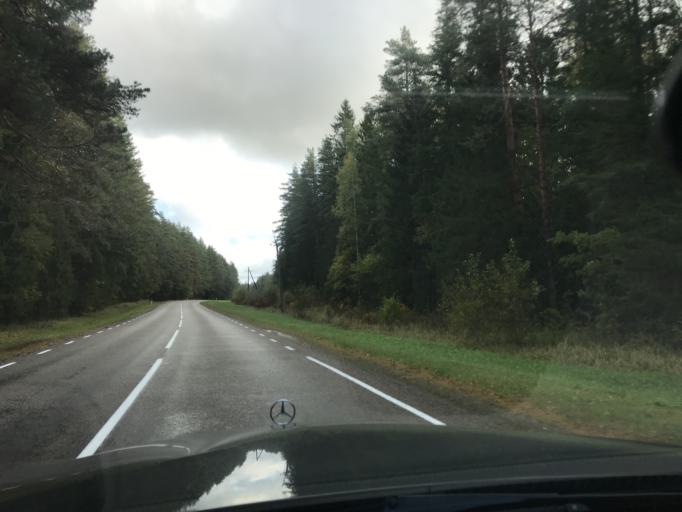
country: EE
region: Valgamaa
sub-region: Torva linn
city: Torva
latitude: 58.0076
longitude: 26.1022
